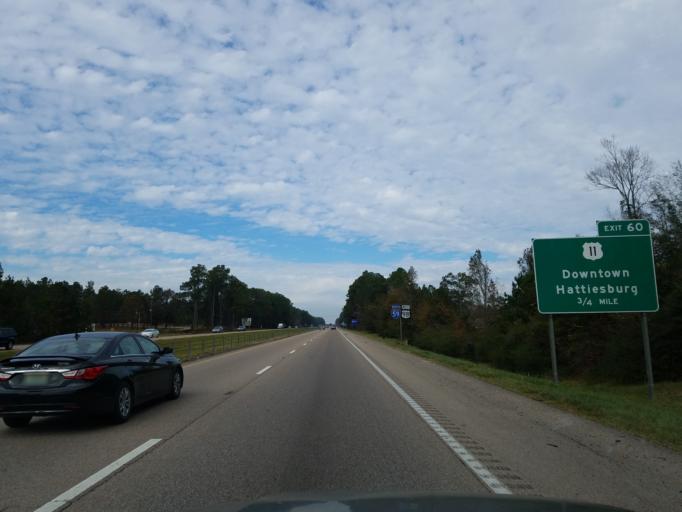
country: US
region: Mississippi
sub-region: Lamar County
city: West Hattiesburg
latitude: 31.2487
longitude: -89.3290
